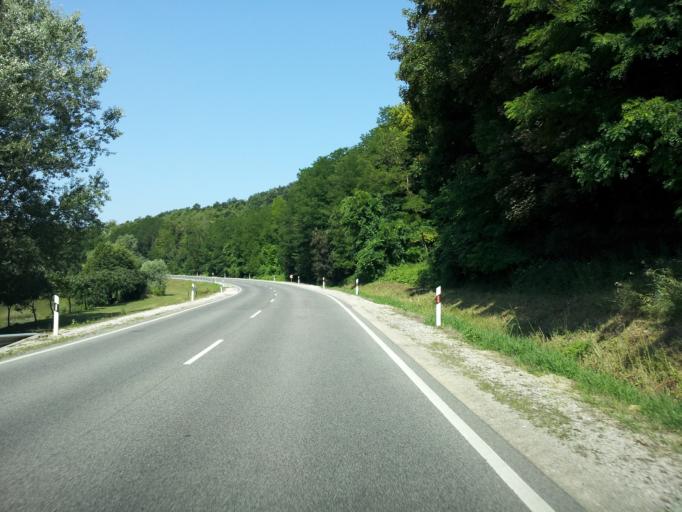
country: HU
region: Zala
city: Heviz
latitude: 46.8086
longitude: 17.0804
